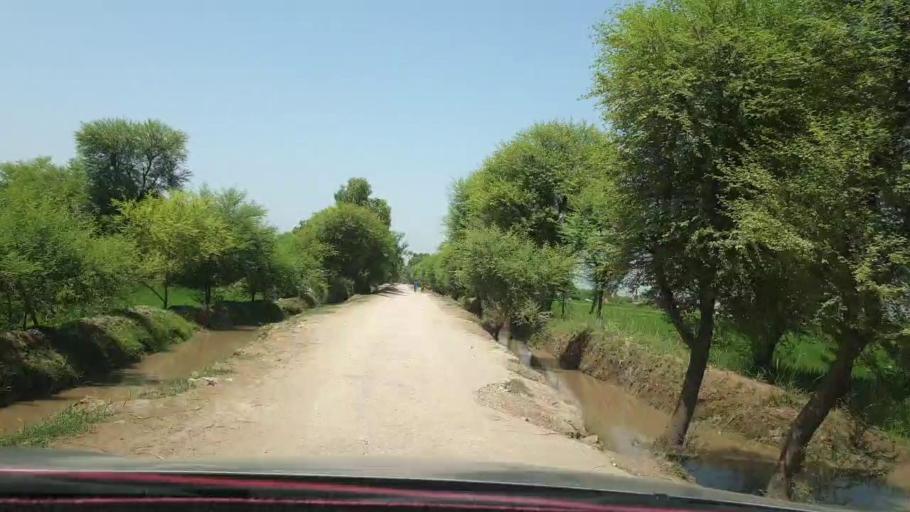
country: PK
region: Sindh
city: Warah
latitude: 27.5240
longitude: 67.8137
